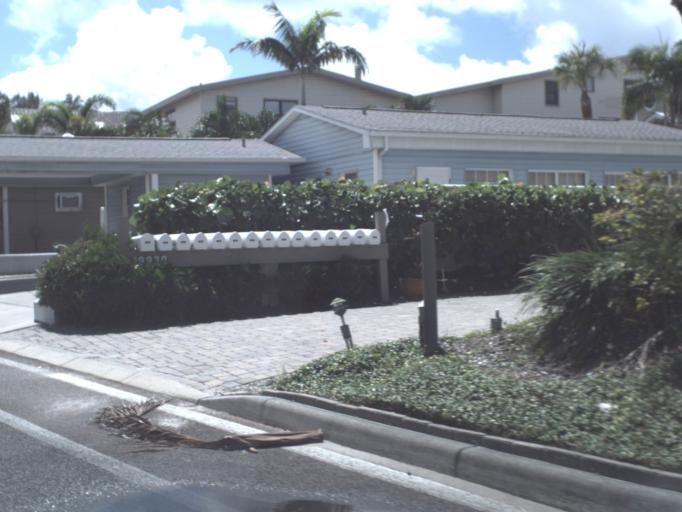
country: US
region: Florida
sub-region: Pinellas County
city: Indian Shores
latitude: 27.8649
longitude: -82.8486
